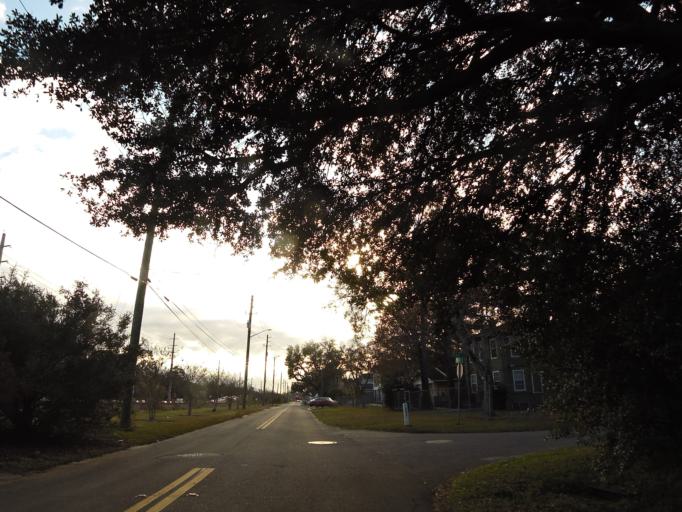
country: US
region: Florida
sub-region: Duval County
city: Jacksonville
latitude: 30.3112
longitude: -81.7085
